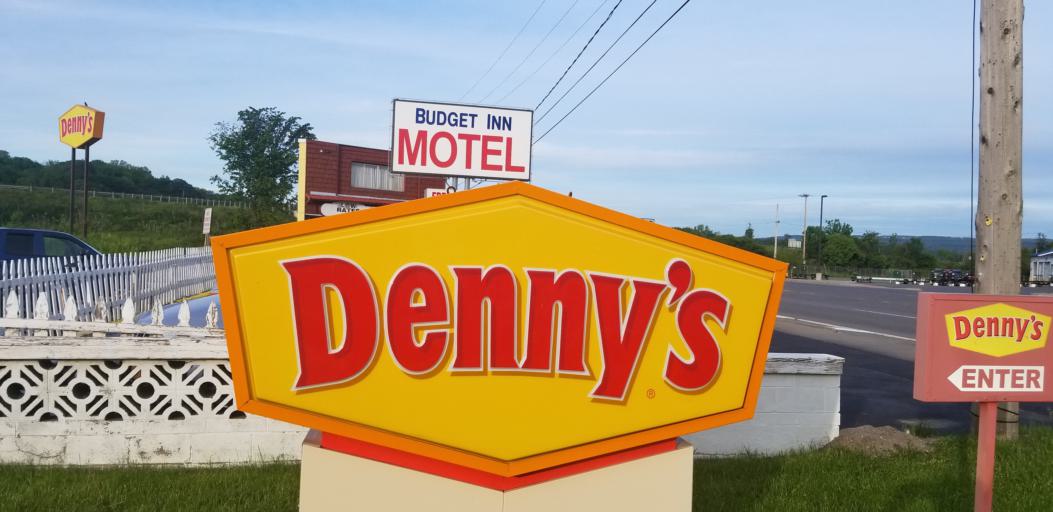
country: US
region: New York
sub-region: Herkimer County
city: Herkimer
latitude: 43.0186
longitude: -74.9923
